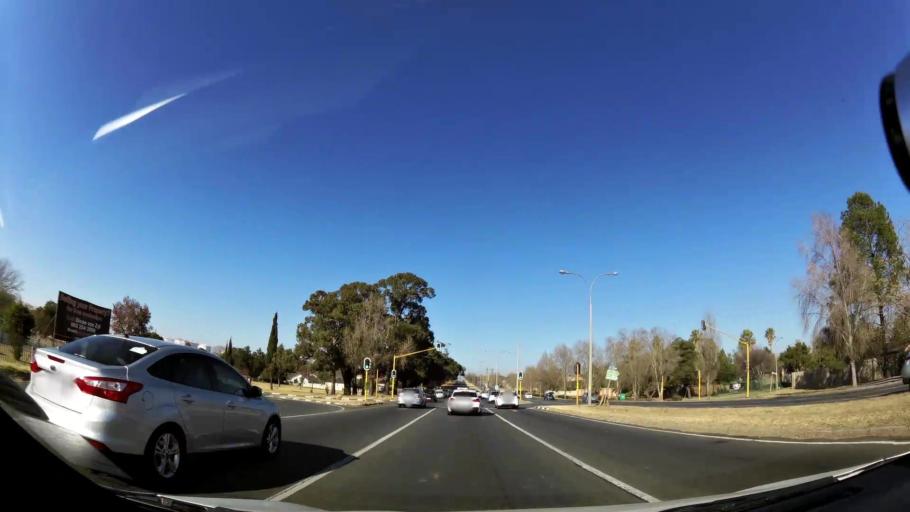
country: ZA
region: Gauteng
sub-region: Ekurhuleni Metropolitan Municipality
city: Germiston
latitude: -26.2922
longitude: 28.1192
